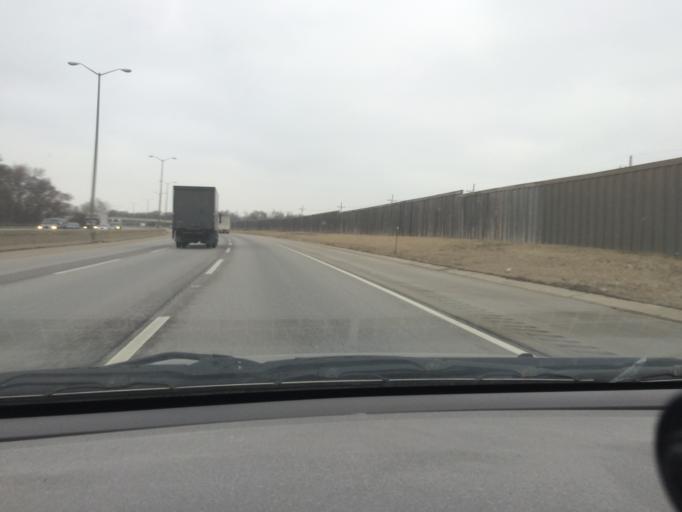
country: US
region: Illinois
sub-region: DuPage County
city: Lombard
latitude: 41.8771
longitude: -88.0329
